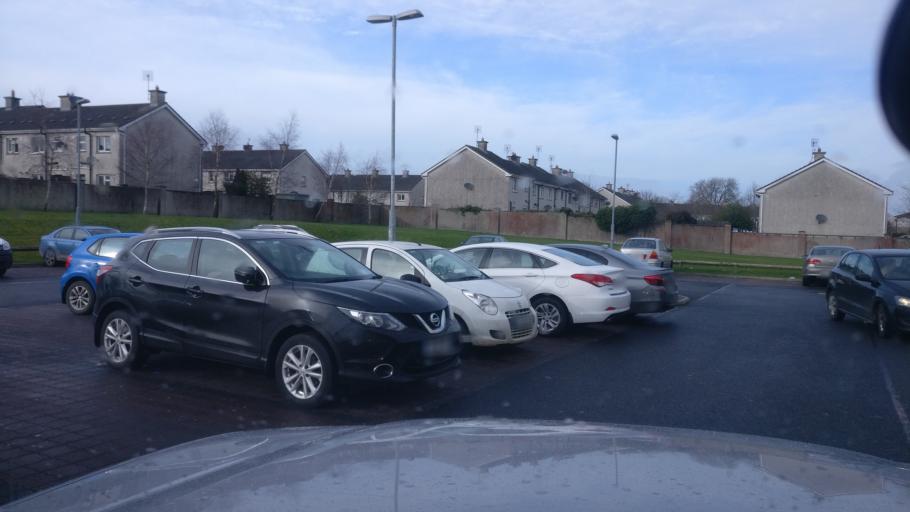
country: IE
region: Leinster
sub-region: Kilkenny
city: Kilkenny
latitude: 52.6636
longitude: -7.2338
